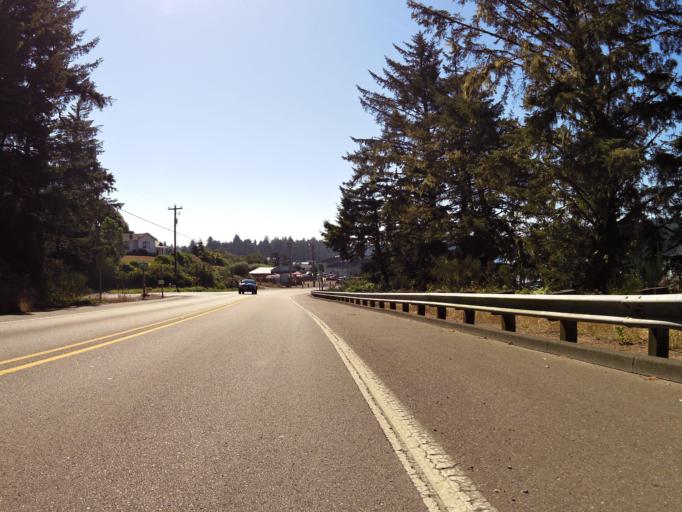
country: US
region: Oregon
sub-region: Coos County
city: Barview
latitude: 43.3401
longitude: -124.3175
